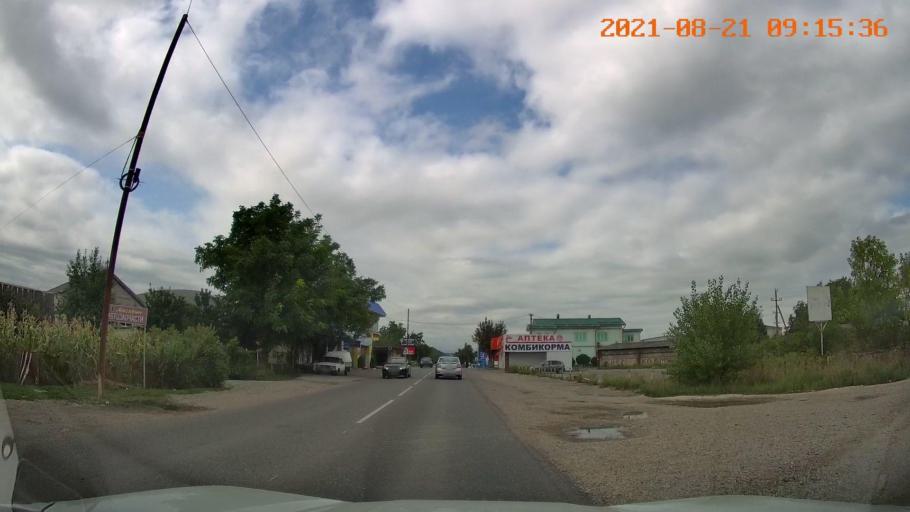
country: RU
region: Stavropol'skiy
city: Svobody
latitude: 43.9926
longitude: 43.0347
